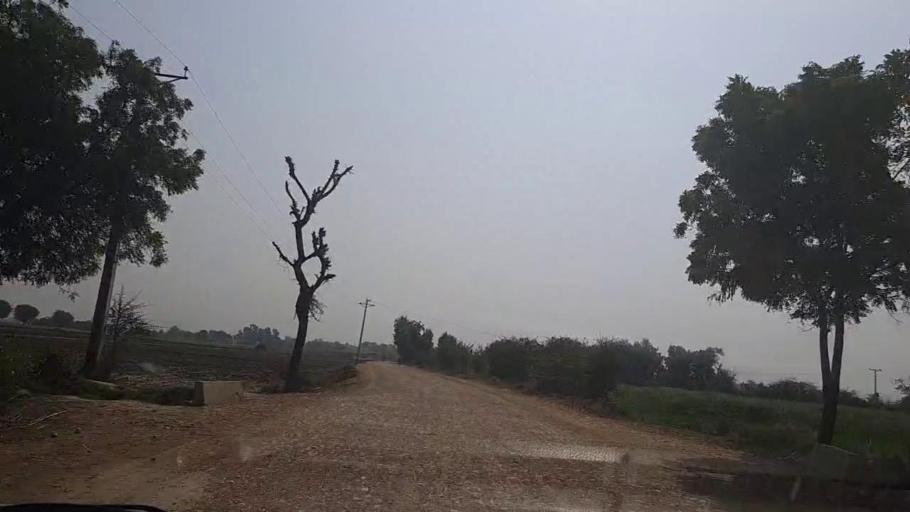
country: PK
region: Sindh
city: Pithoro
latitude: 25.5526
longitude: 69.2484
